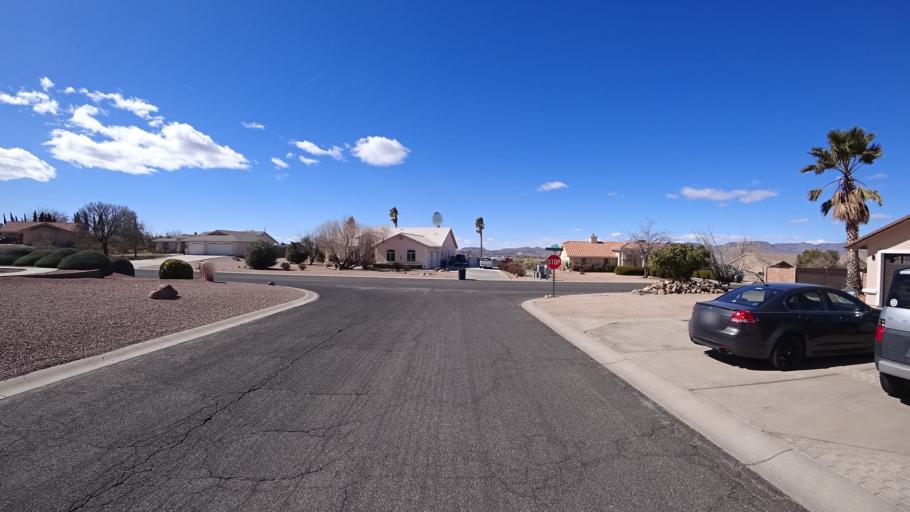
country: US
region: Arizona
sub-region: Mohave County
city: Kingman
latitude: 35.1977
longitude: -113.9750
